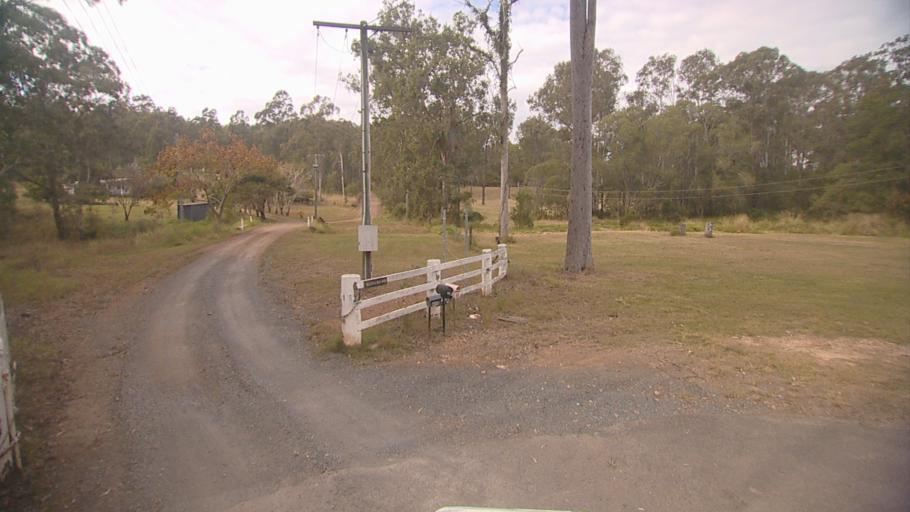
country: AU
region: Queensland
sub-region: Logan
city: Windaroo
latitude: -27.7615
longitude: 153.1546
